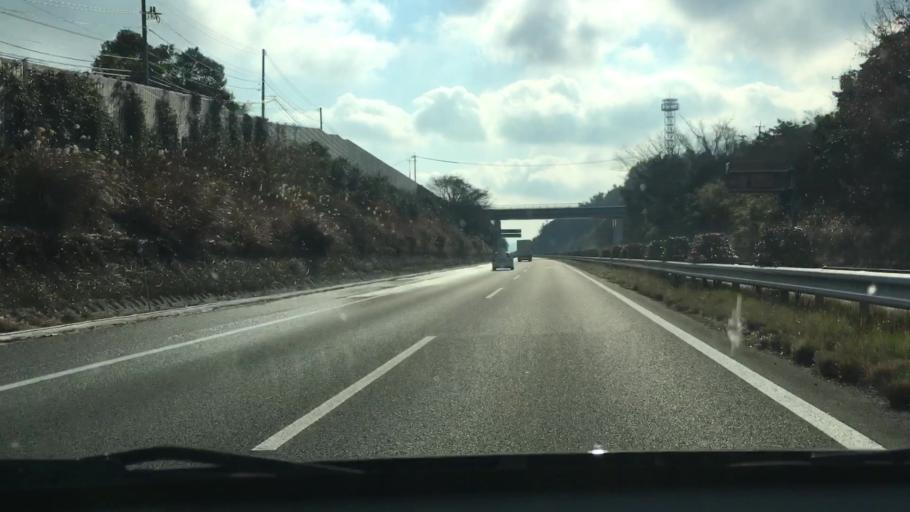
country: JP
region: Kumamoto
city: Kumamoto
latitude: 32.7293
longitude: 130.7742
